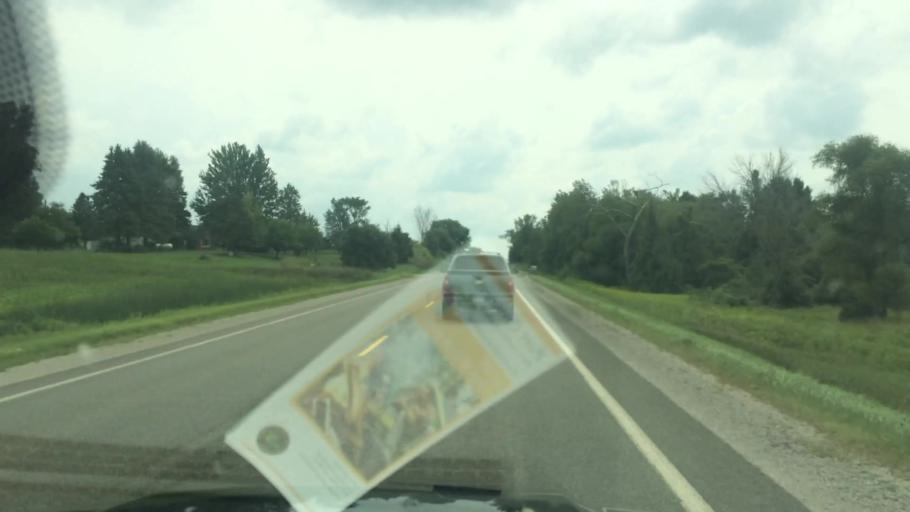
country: US
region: Michigan
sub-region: Tuscola County
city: Cass City
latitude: 43.6820
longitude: -83.0982
